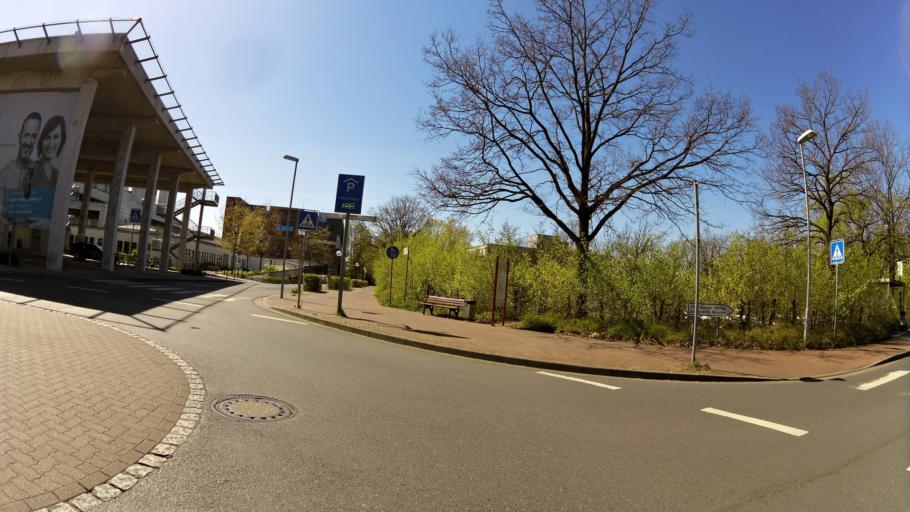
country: DE
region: Lower Saxony
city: Rotenburg
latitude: 53.1058
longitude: 9.4115
